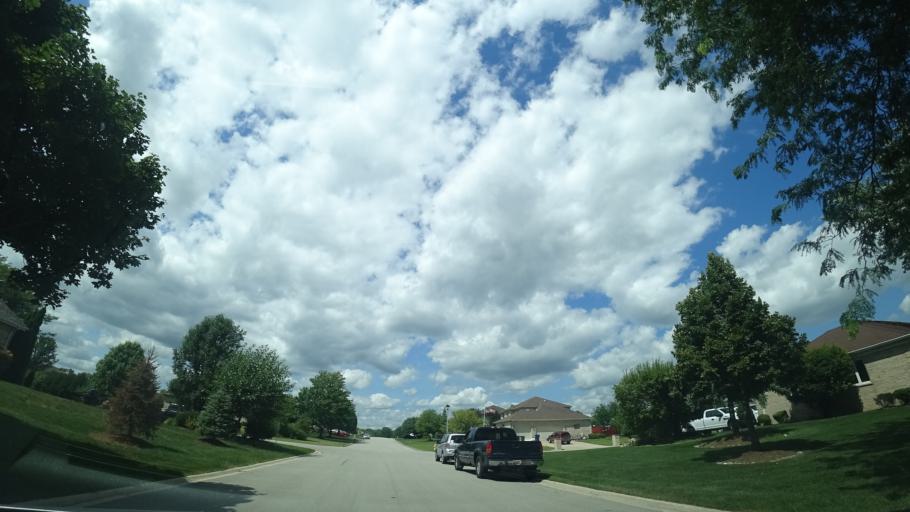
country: US
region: Illinois
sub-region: Will County
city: Homer Glen
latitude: 41.5814
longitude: -87.9142
